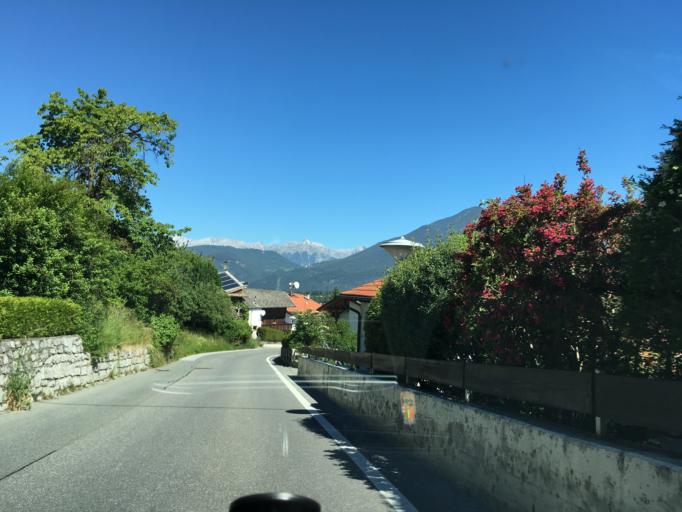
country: AT
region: Tyrol
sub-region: Politischer Bezirk Innsbruck Land
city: Oberperfuss
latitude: 47.2422
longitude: 11.2484
